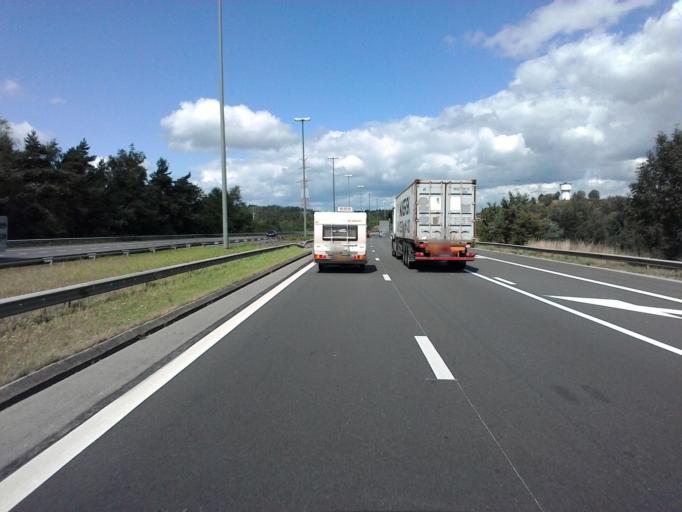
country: BE
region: Wallonia
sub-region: Province du Luxembourg
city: Arlon
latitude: 49.6738
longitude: 5.7706
